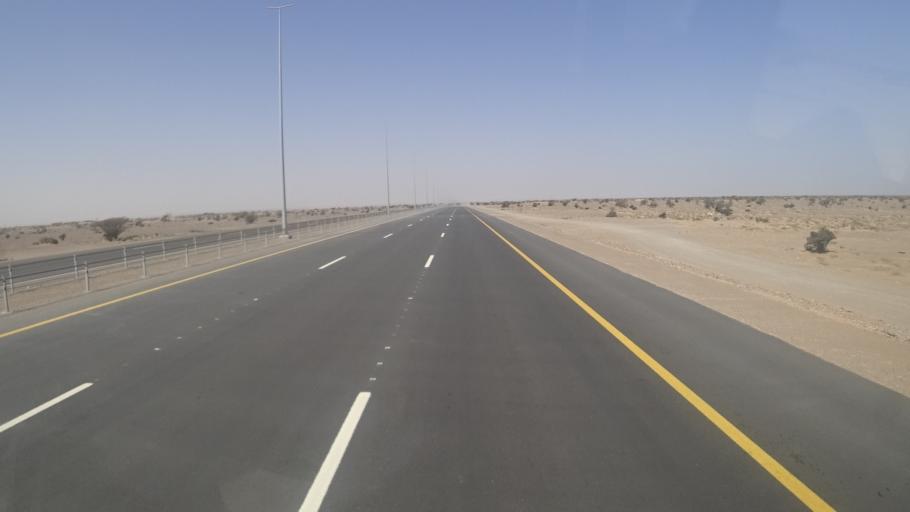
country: OM
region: Ash Sharqiyah
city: Sur
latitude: 22.2744
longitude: 59.2144
